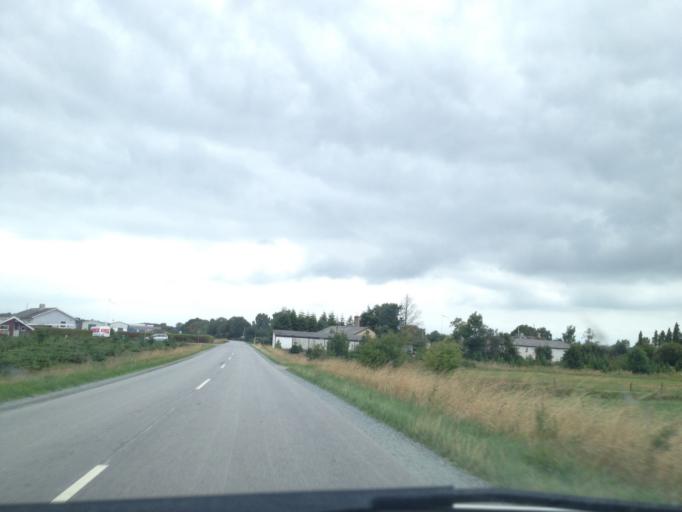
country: DK
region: South Denmark
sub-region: Kolding Kommune
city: Christiansfeld
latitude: 55.3072
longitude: 9.5104
